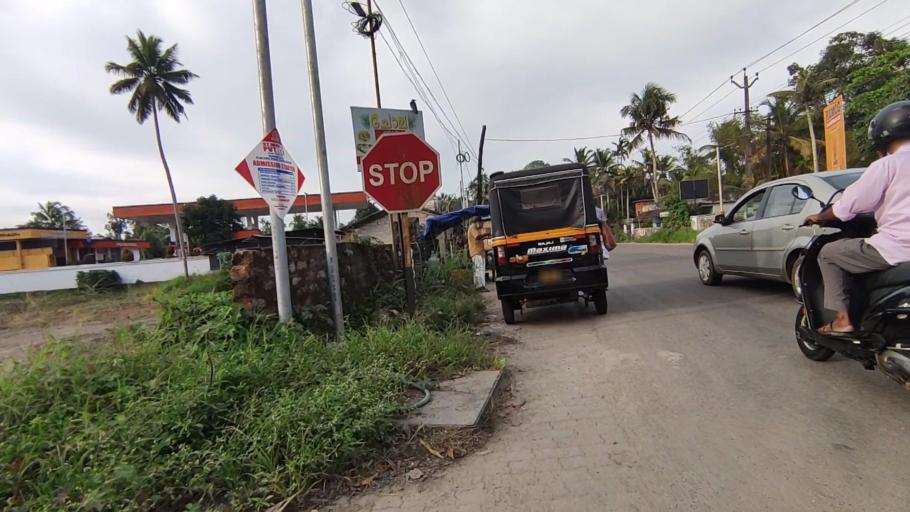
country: IN
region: Kerala
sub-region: Kottayam
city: Kottayam
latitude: 9.6240
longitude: 76.5123
